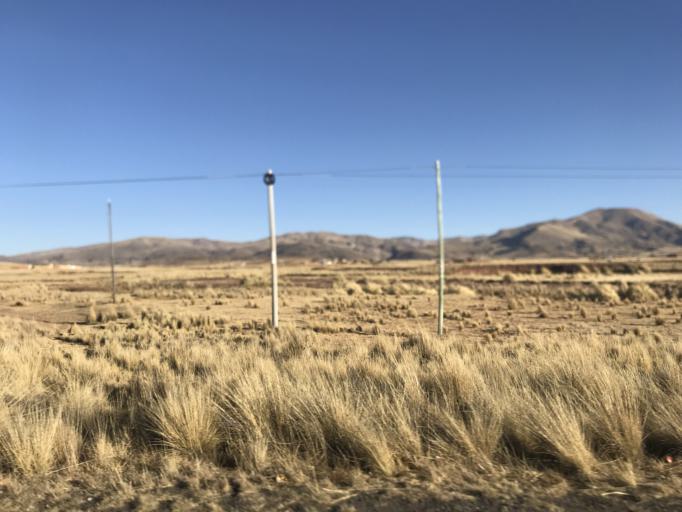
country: BO
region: La Paz
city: Tiahuanaco
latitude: -16.5671
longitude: -68.6499
